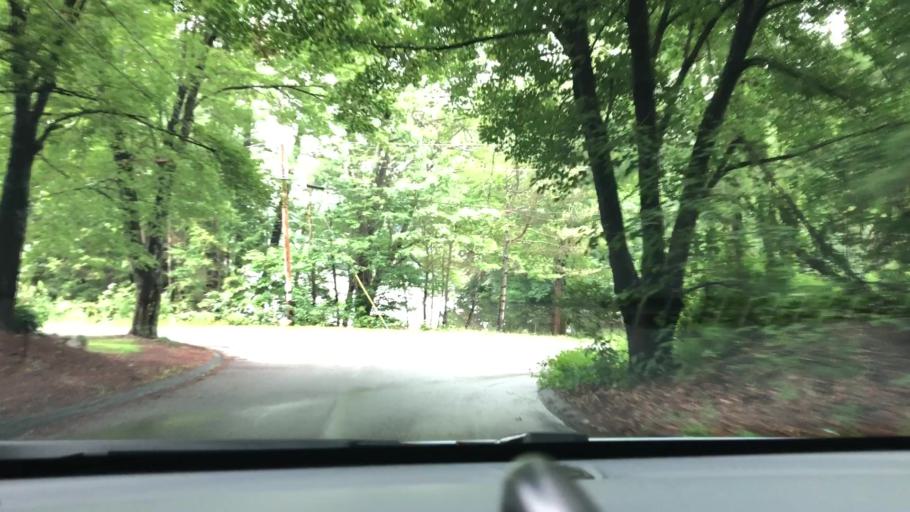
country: US
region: New Hampshire
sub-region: Hillsborough County
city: Pinardville
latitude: 43.0069
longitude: -71.5180
